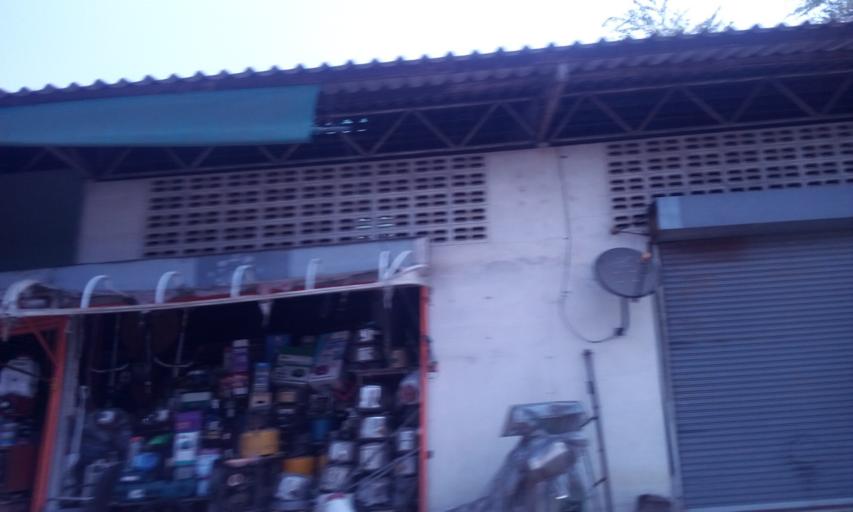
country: TH
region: Chachoengsao
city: Bang Nam Priao
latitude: 13.9652
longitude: 100.9658
